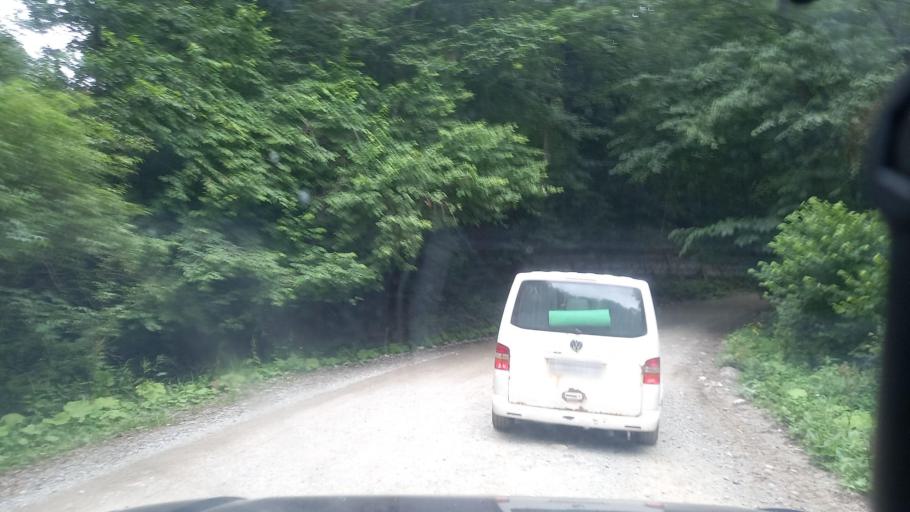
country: RU
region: Karachayevo-Cherkesiya
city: Kurdzhinovo
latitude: 43.8581
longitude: 40.9373
